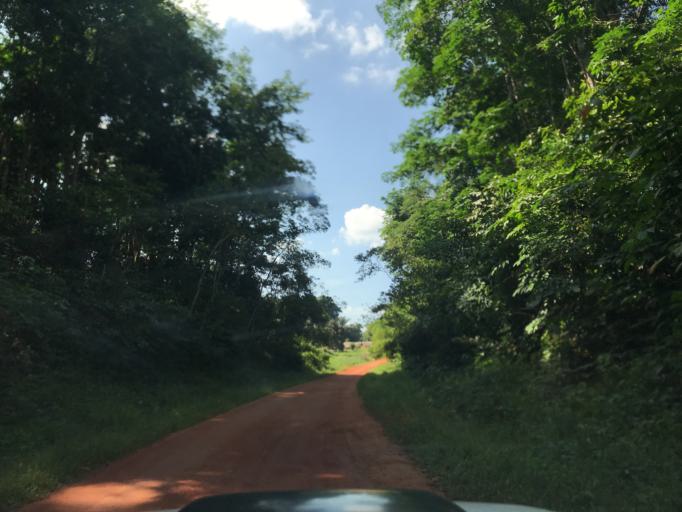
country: CD
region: Eastern Province
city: Kisangani
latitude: 1.1789
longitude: 25.2480
